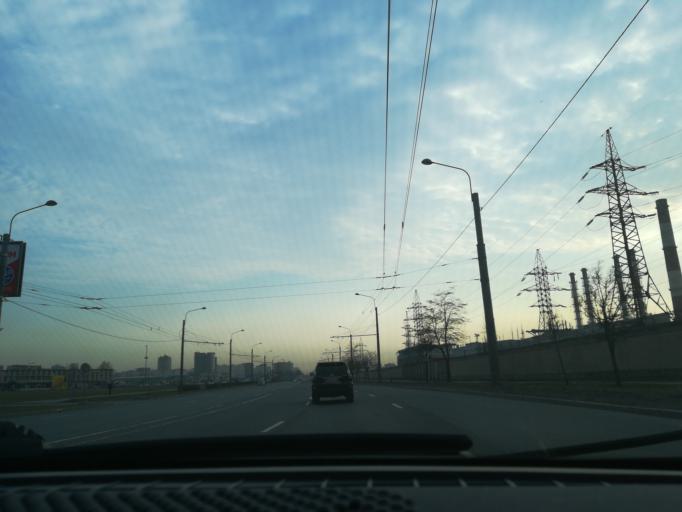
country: RU
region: St.-Petersburg
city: Avtovo
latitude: 59.8724
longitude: 30.2515
